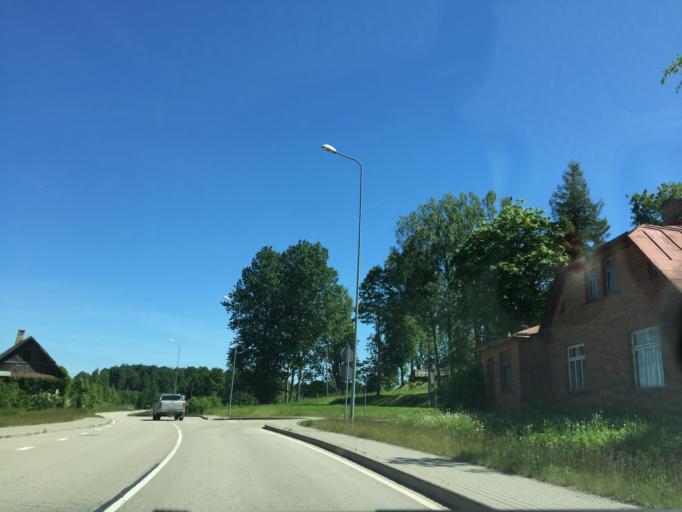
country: LV
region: Preilu Rajons
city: Jaunaglona
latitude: 56.2351
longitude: 27.2297
